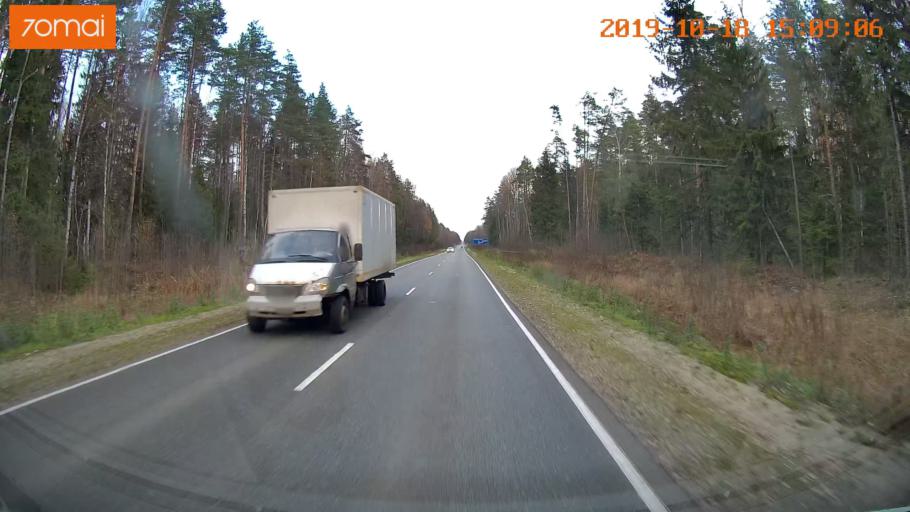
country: RU
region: Vladimir
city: Gus'-Khrustal'nyy
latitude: 55.5616
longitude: 40.6176
